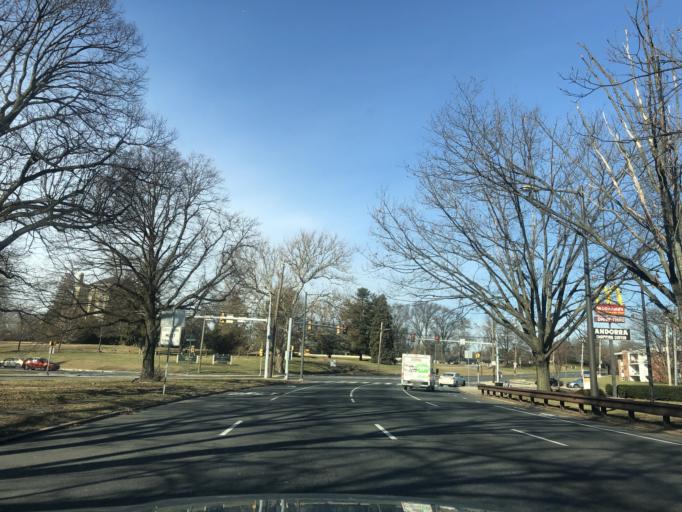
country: US
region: Pennsylvania
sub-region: Montgomery County
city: Flourtown
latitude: 40.0635
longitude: -75.2390
